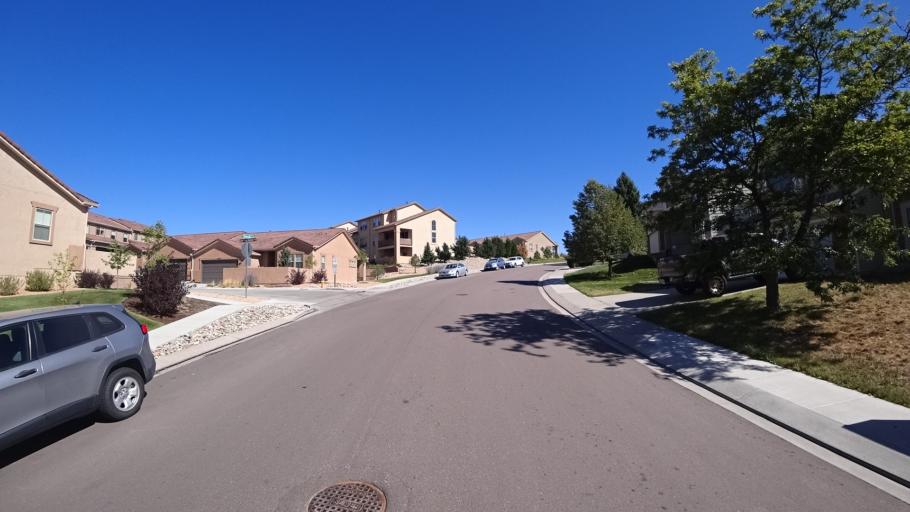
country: US
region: Colorado
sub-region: El Paso County
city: Black Forest
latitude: 38.9527
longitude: -104.7370
